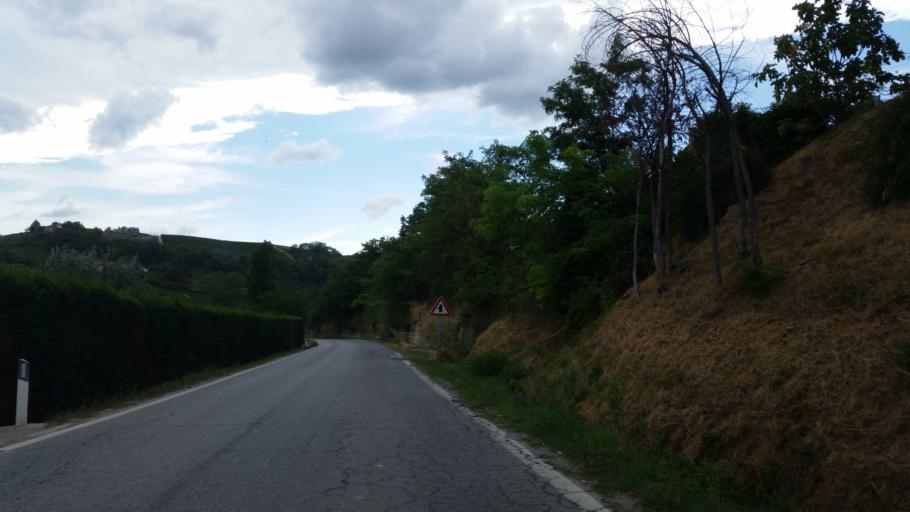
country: IT
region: Piedmont
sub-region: Provincia di Cuneo
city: Mango
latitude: 44.6816
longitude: 8.1439
